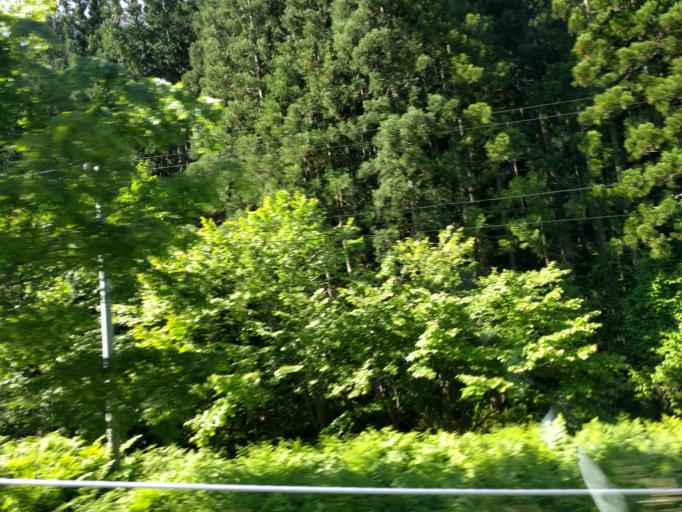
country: JP
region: Fukushima
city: Kitakata
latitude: 37.3783
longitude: 139.8335
